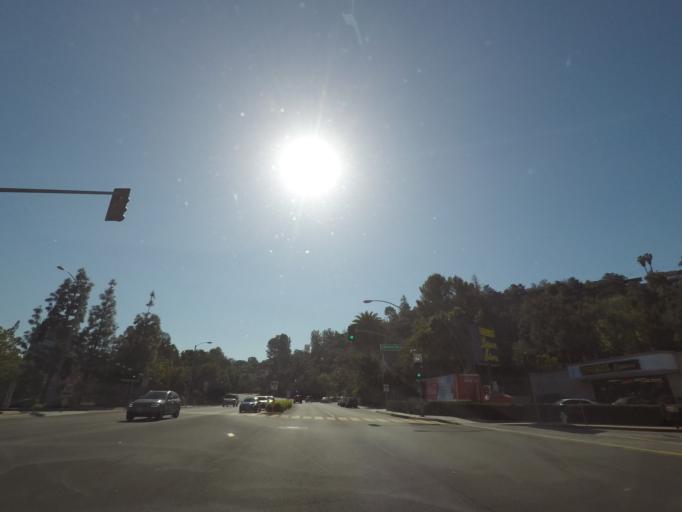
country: US
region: California
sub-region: Los Angeles County
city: South Pasadena
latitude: 34.1118
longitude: -118.1699
